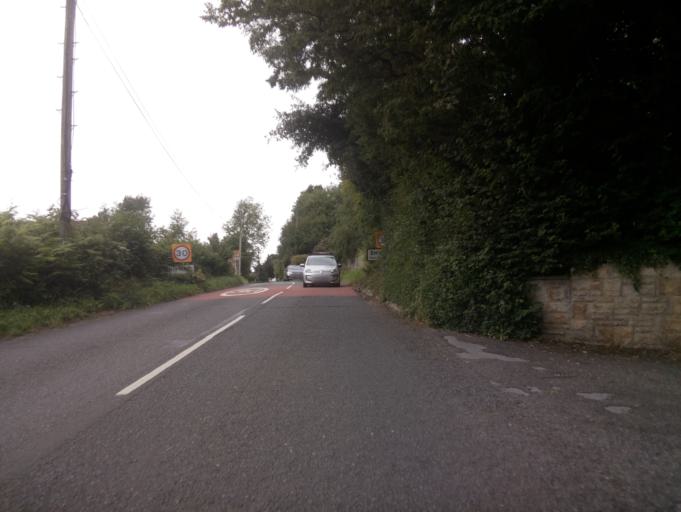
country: GB
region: England
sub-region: North Somerset
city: Churchill
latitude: 51.3081
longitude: -2.7983
